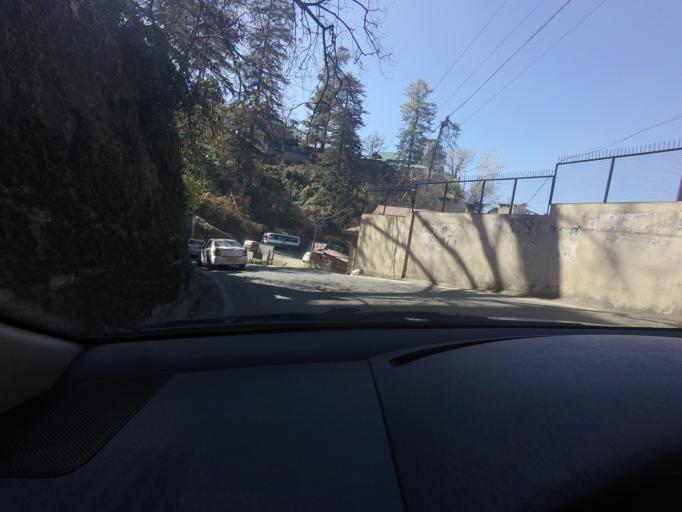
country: IN
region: Himachal Pradesh
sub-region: Shimla
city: Shimla
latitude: 31.1087
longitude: 77.1674
